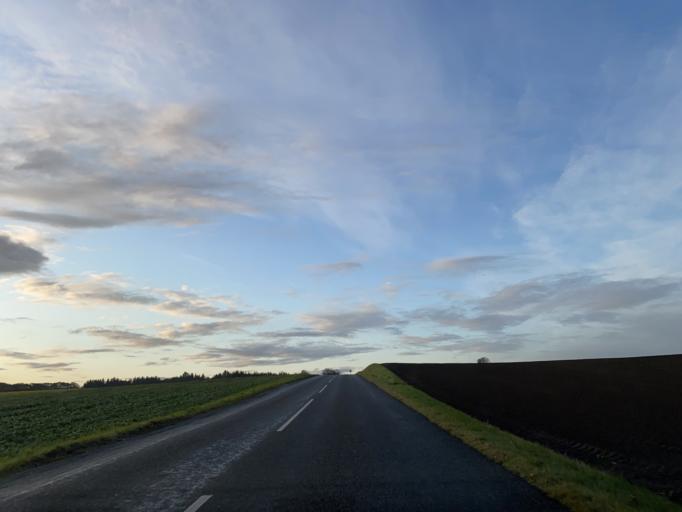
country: DK
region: Central Jutland
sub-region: Favrskov Kommune
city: Hammel
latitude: 56.2105
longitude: 9.7523
